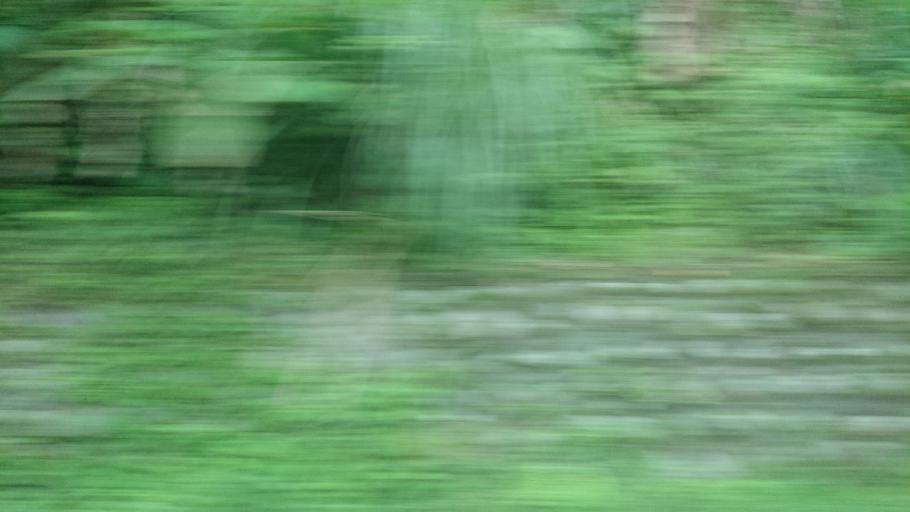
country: TW
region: Taiwan
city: Daxi
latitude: 24.8885
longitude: 121.3771
